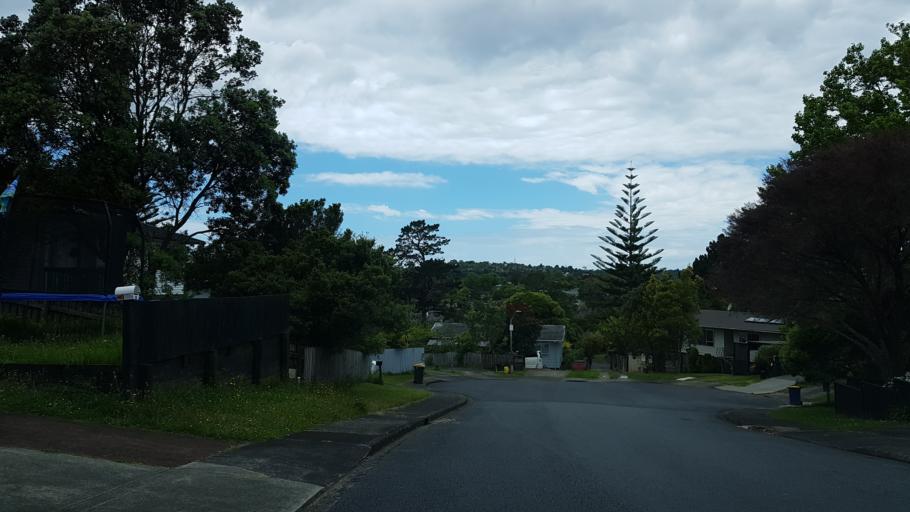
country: NZ
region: Auckland
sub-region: Auckland
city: North Shore
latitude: -36.7954
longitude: 174.6941
